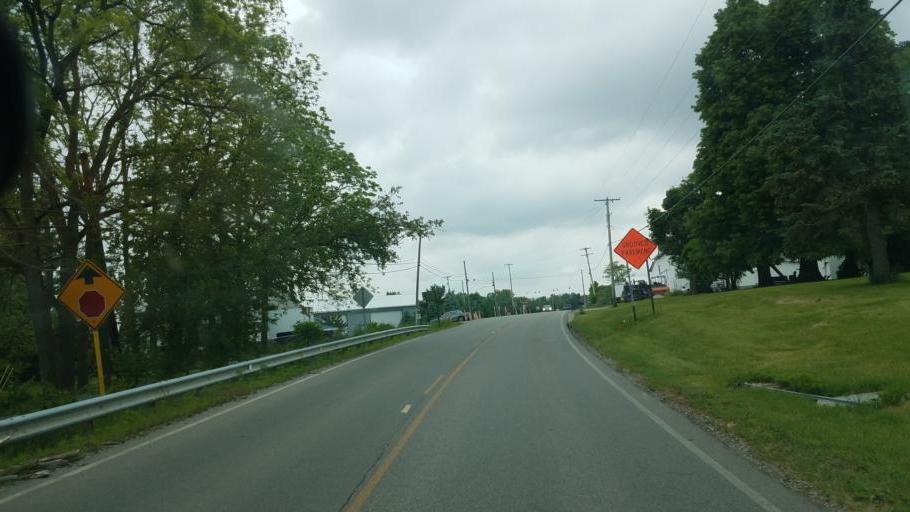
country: US
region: Ohio
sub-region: Delaware County
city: Delaware
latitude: 40.3189
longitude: -83.1235
